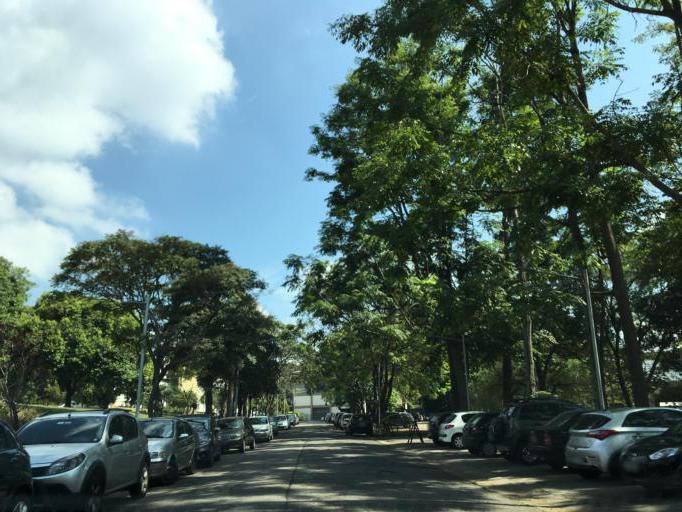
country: BR
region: Sao Paulo
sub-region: Osasco
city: Osasco
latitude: -23.5606
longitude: -46.7331
